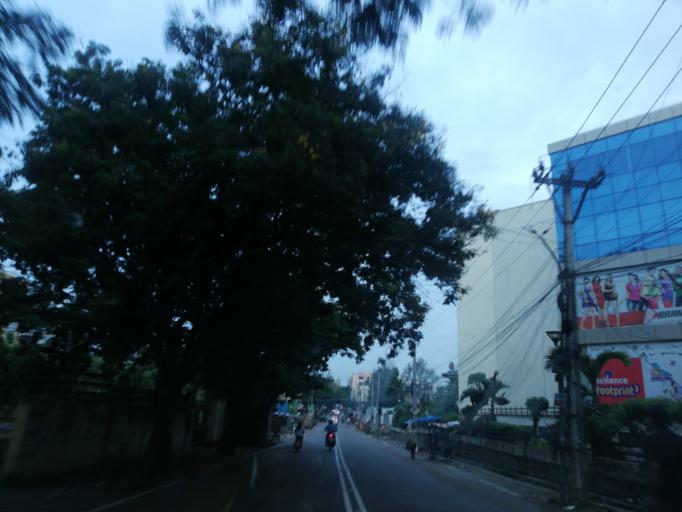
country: IN
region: Telangana
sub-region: Rangareddi
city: Kukatpalli
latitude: 17.4834
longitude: 78.3931
